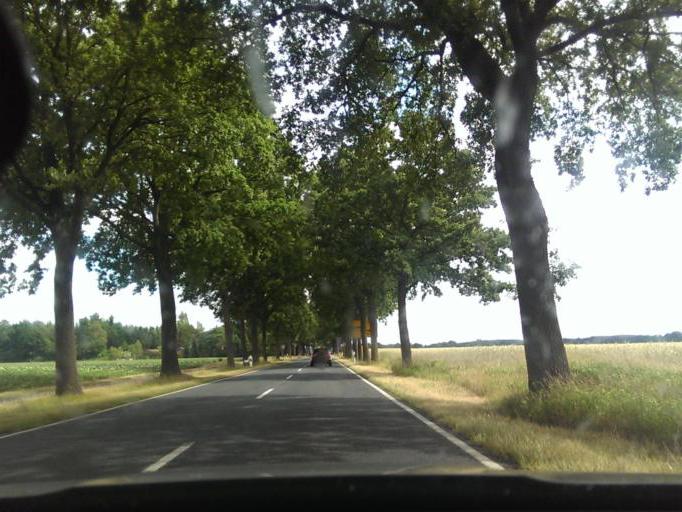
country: DE
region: Lower Saxony
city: Essel
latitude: 52.6836
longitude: 9.6482
